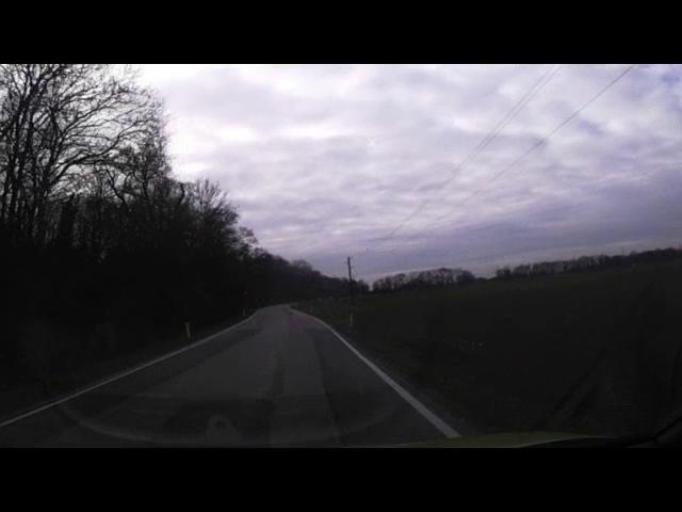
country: AT
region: Lower Austria
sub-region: Politischer Bezirk Baden
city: Pottendorf
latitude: 47.9163
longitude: 16.3831
